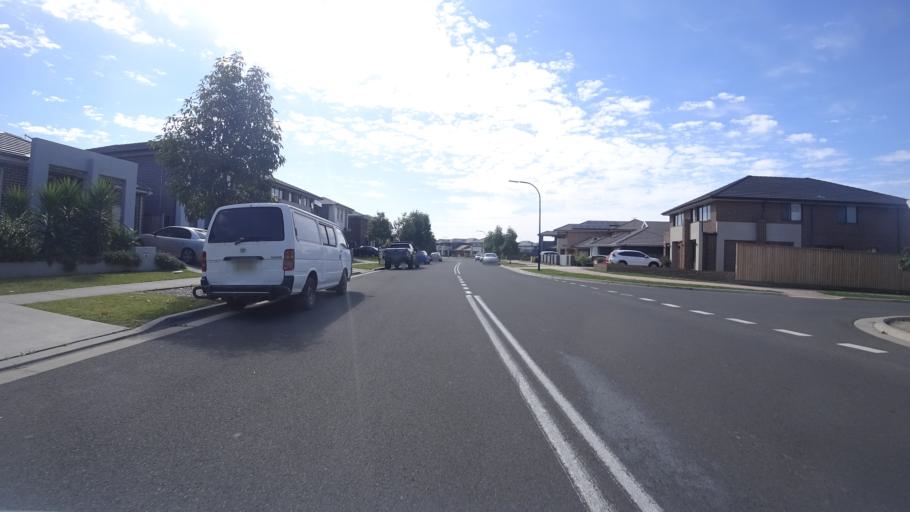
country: AU
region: New South Wales
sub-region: Bankstown
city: Milperra
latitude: -33.9341
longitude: 150.9582
